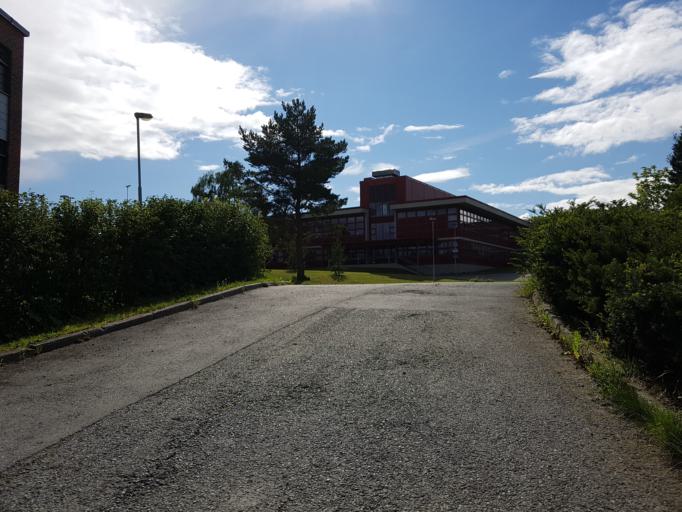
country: NO
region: Sor-Trondelag
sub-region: Trondheim
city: Trondheim
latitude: 63.4189
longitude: 10.4796
